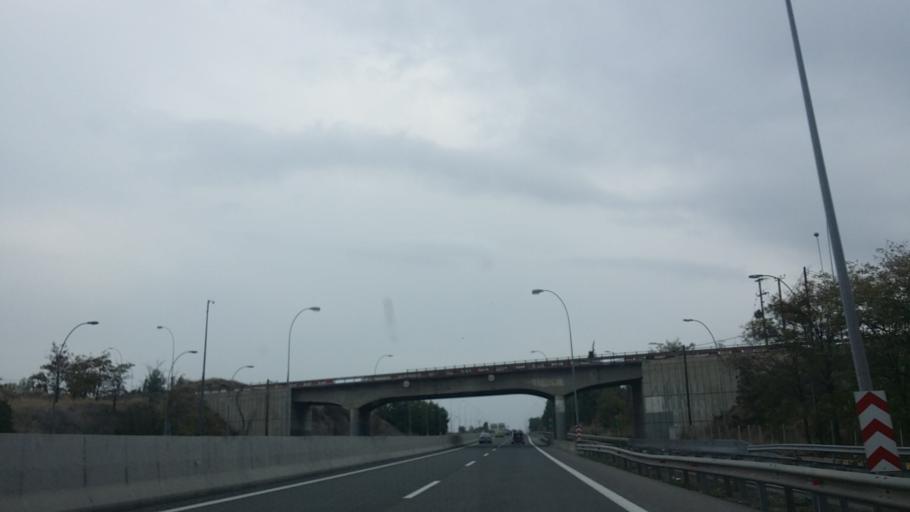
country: GR
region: Central Greece
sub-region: Nomos Voiotias
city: Arma
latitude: 38.3795
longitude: 23.4849
